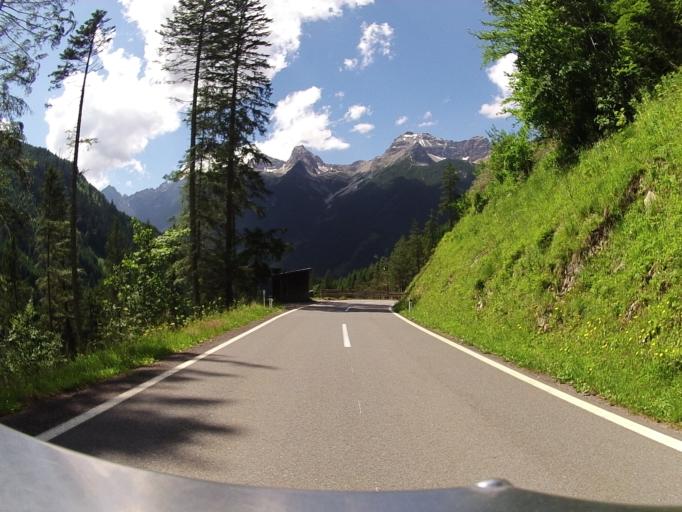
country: AT
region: Tyrol
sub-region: Politischer Bezirk Reutte
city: Elmen
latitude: 47.3225
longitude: 10.5410
